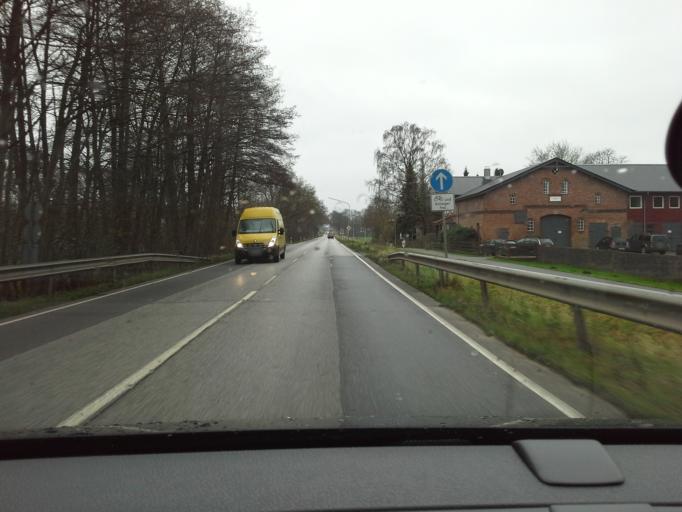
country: DE
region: Schleswig-Holstein
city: Bilsen
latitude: 53.7473
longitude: 9.8863
